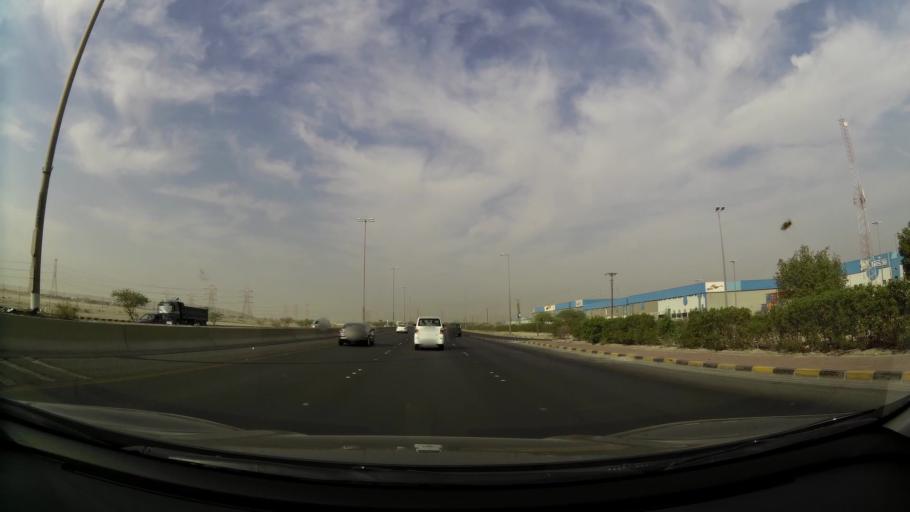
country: KW
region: Al Asimah
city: Ar Rabiyah
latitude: 29.2654
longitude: 47.8539
